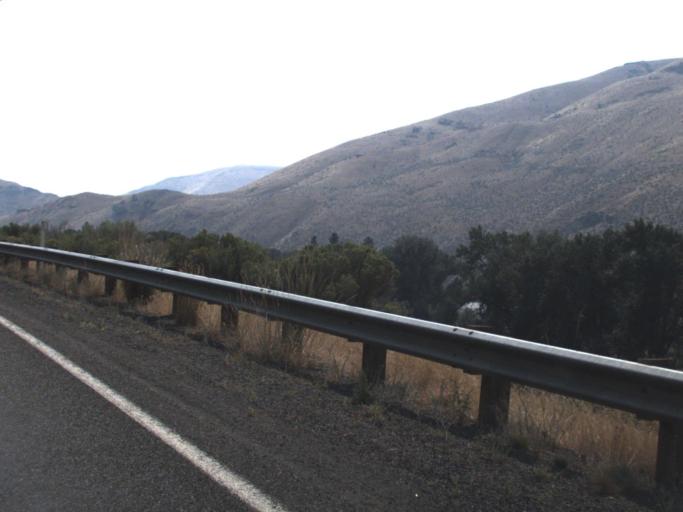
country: US
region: Washington
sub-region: Kittitas County
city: Ellensburg
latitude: 46.9147
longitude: -120.5075
